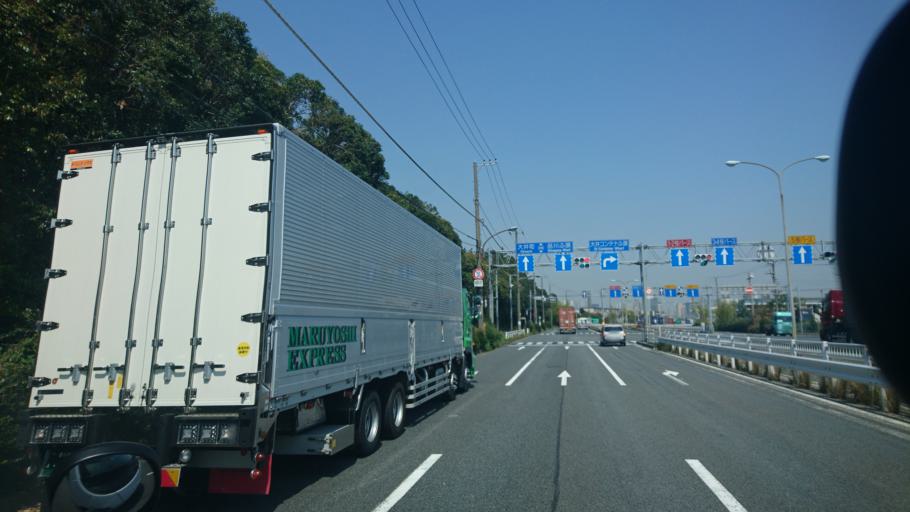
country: JP
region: Kanagawa
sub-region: Kawasaki-shi
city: Kawasaki
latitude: 35.5973
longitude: 139.7633
